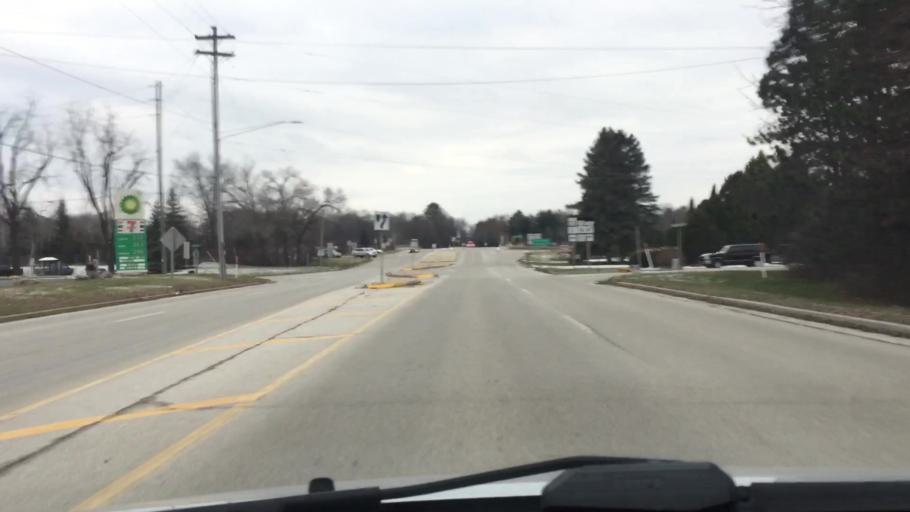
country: US
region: Wisconsin
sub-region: Waukesha County
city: Okauchee Lake
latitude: 43.1101
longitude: -88.4613
